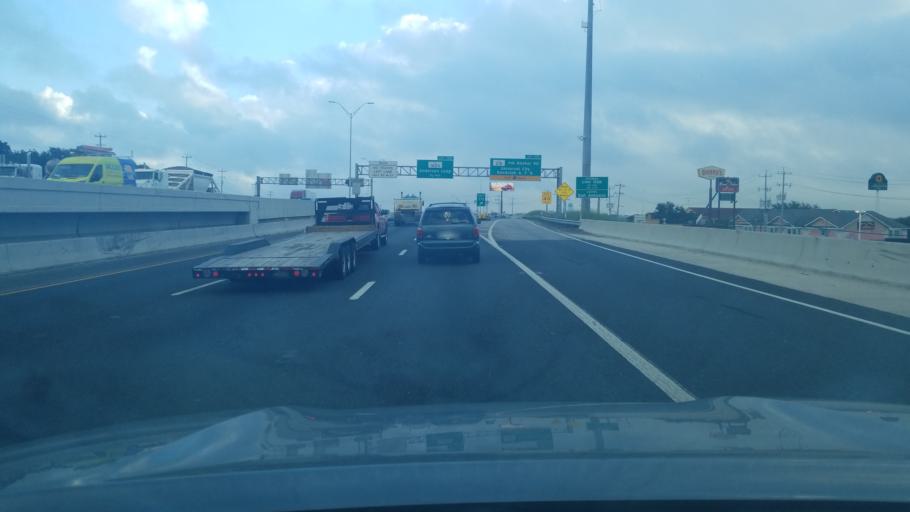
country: US
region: Texas
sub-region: Bexar County
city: Live Oak
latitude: 29.5557
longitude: -98.3466
